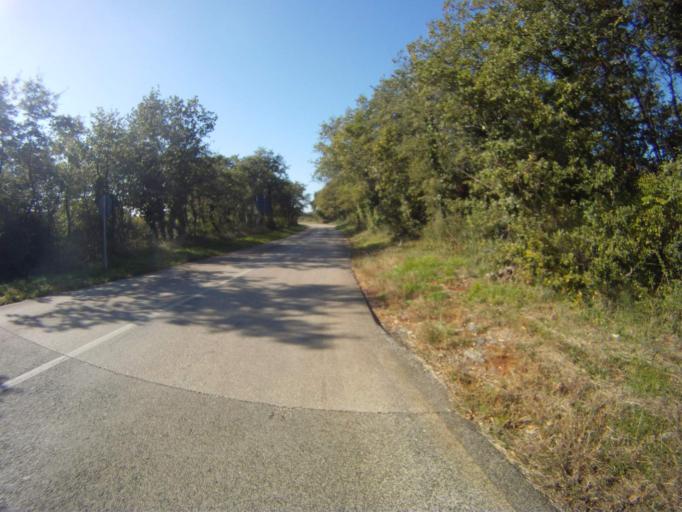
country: HR
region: Istarska
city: Umag
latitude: 45.3849
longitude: 13.5447
